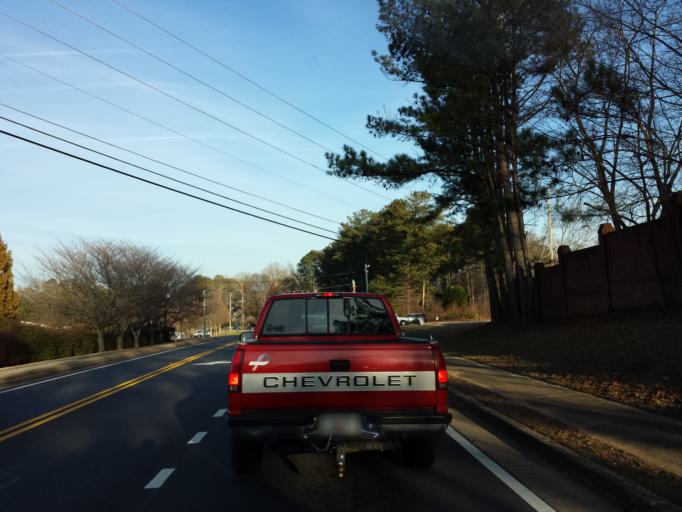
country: US
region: Georgia
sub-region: Cobb County
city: Marietta
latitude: 33.9829
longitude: -84.4634
